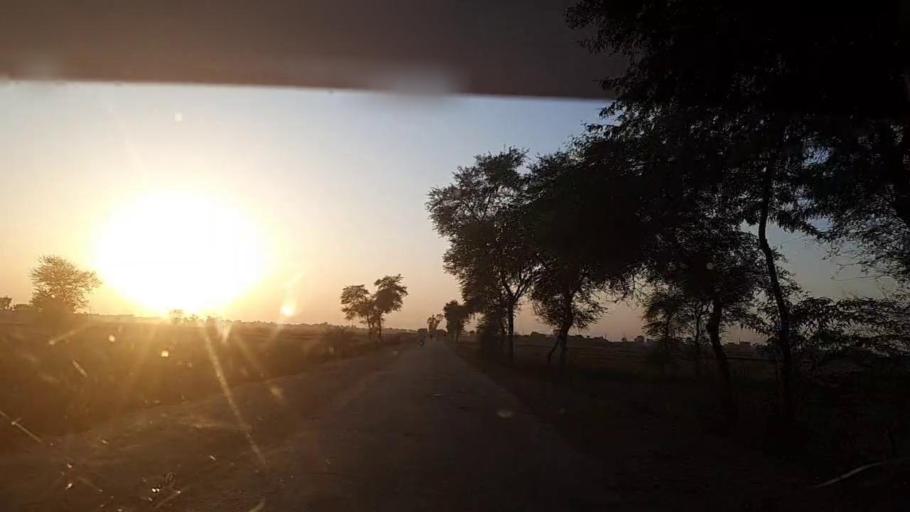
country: PK
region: Sindh
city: Ratodero
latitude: 27.8913
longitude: 68.2400
